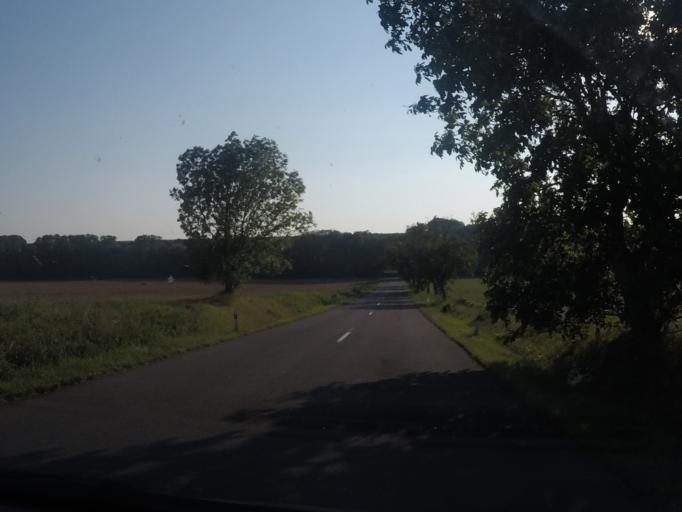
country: SK
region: Nitriansky
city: Zlate Moravce
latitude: 48.3866
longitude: 18.3508
